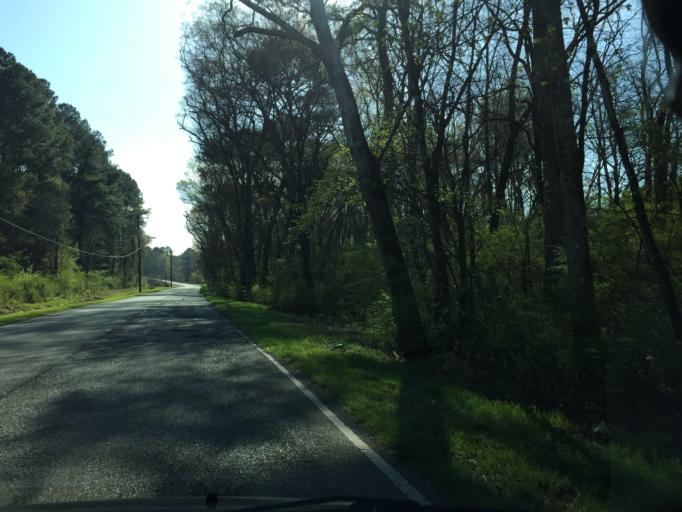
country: US
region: Tennessee
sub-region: Hamilton County
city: East Chattanooga
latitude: 35.0684
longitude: -85.2173
